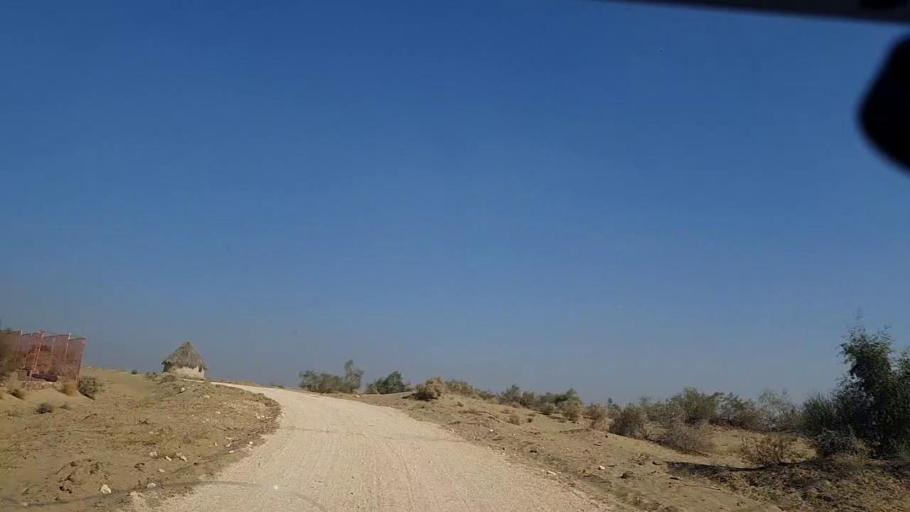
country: PK
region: Sindh
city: Khanpur
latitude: 27.5586
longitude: 69.4006
